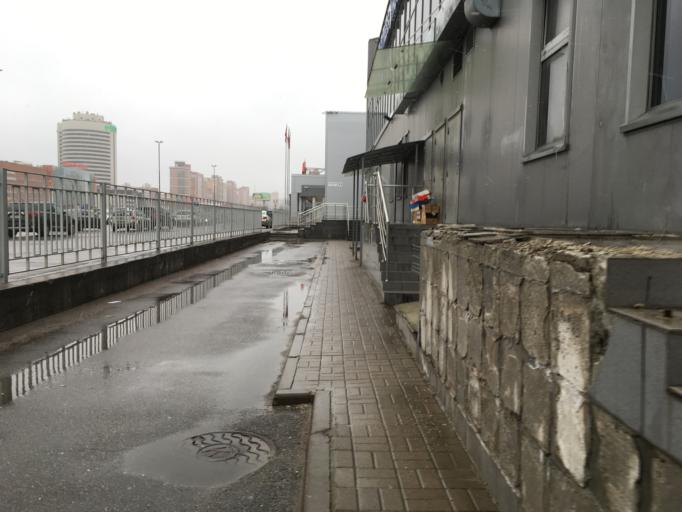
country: RU
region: St.-Petersburg
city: Komendantsky aerodrom
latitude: 60.0007
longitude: 30.2662
